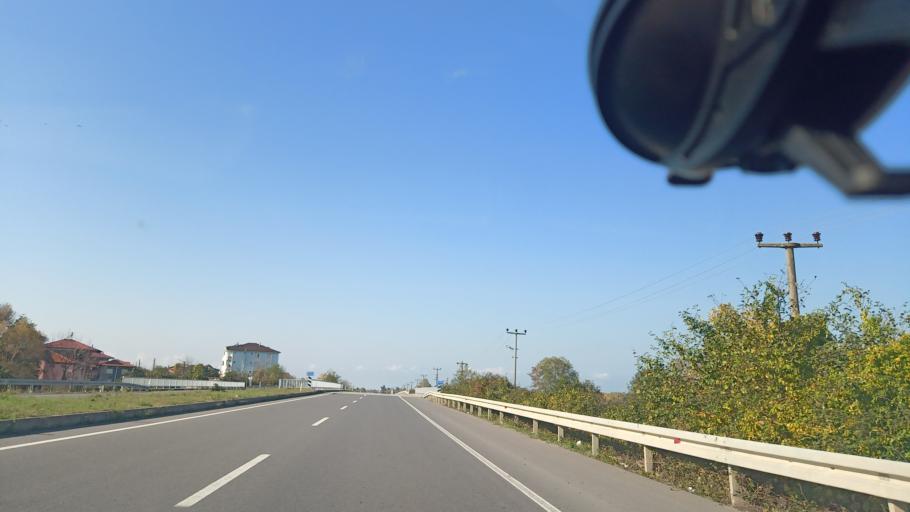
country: TR
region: Sakarya
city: Karasu
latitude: 41.0729
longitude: 30.7894
